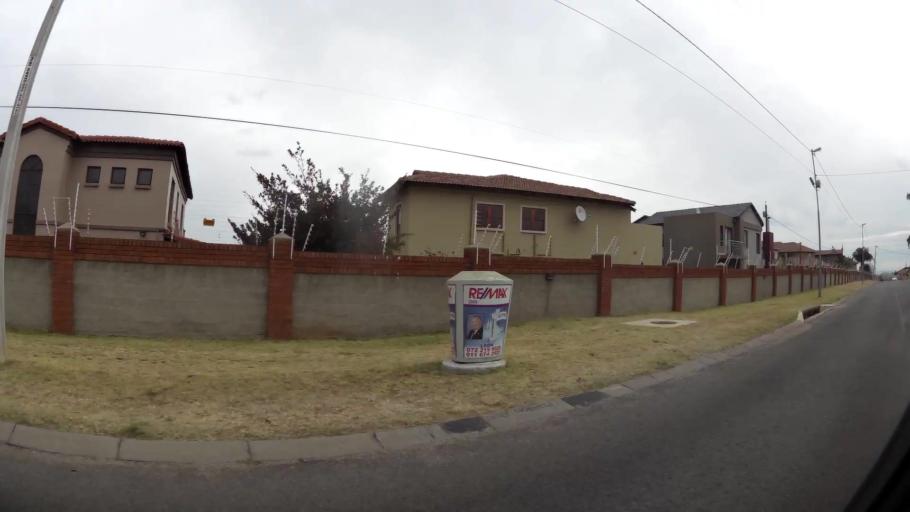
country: ZA
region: Gauteng
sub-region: City of Johannesburg Metropolitan Municipality
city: Roodepoort
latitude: -26.1041
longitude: 27.9015
